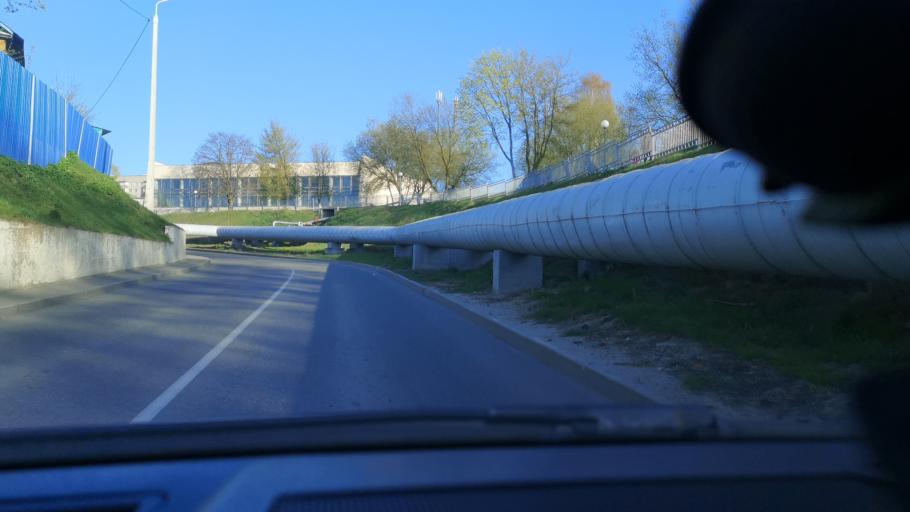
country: BY
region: Gomel
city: Gomel
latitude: 52.4508
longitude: 31.0103
